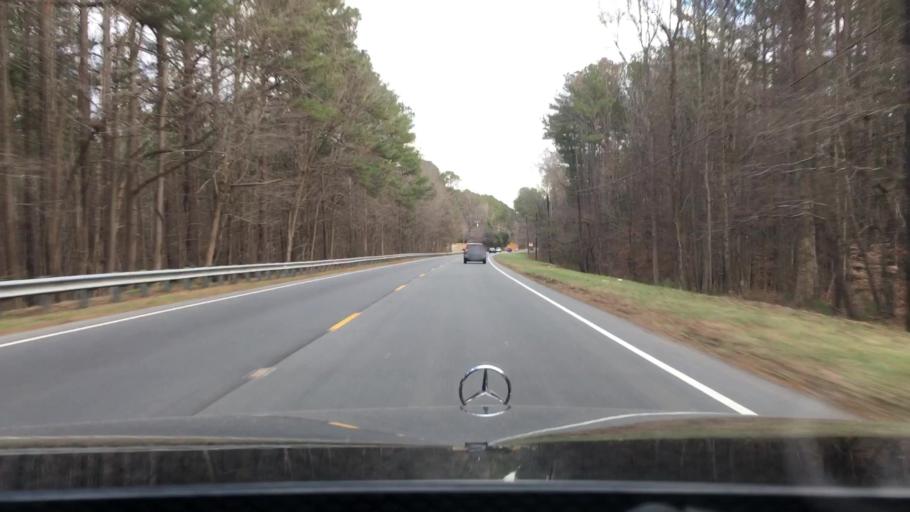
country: US
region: North Carolina
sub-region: Orange County
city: Hillsborough
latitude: 36.0504
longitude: -79.0328
